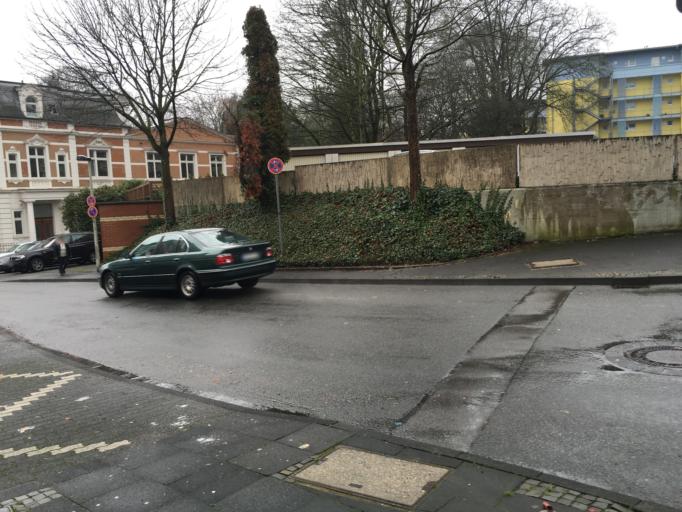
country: DE
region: North Rhine-Westphalia
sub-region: Regierungsbezirk Dusseldorf
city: Solingen
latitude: 51.1690
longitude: 7.0847
